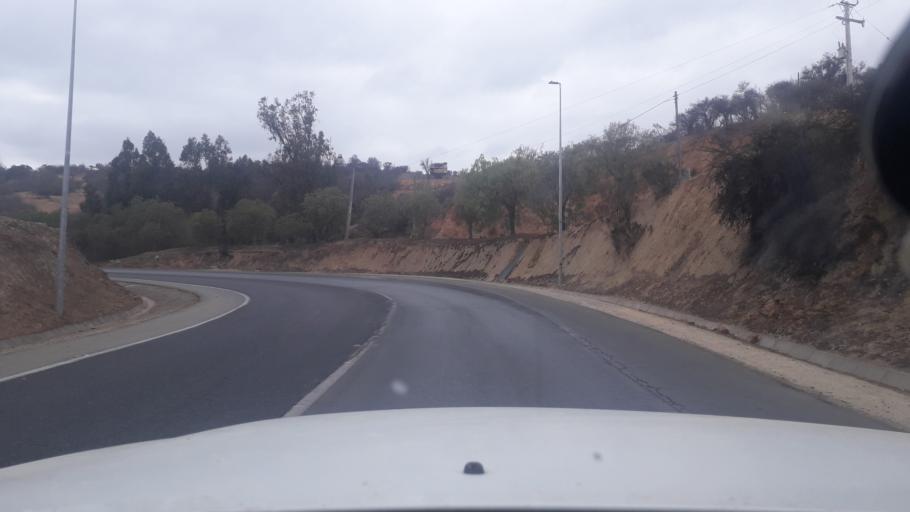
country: CL
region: Valparaiso
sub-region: Provincia de Marga Marga
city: Villa Alemana
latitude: -33.0525
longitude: -71.3322
